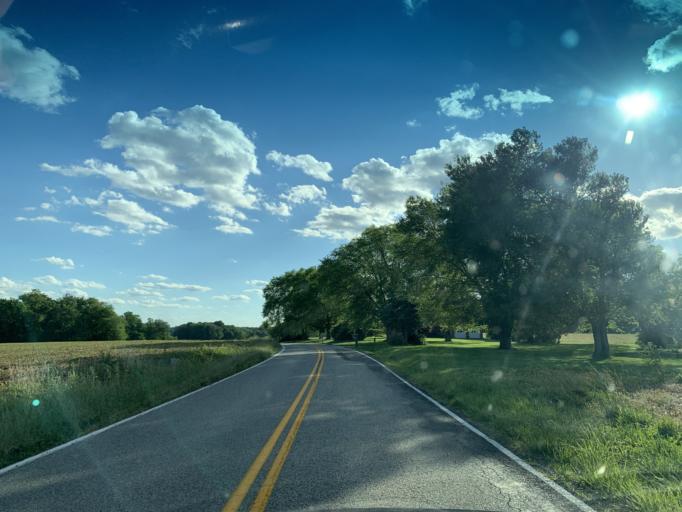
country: US
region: Maryland
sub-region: Cecil County
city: Rising Sun
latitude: 39.6613
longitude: -76.0252
